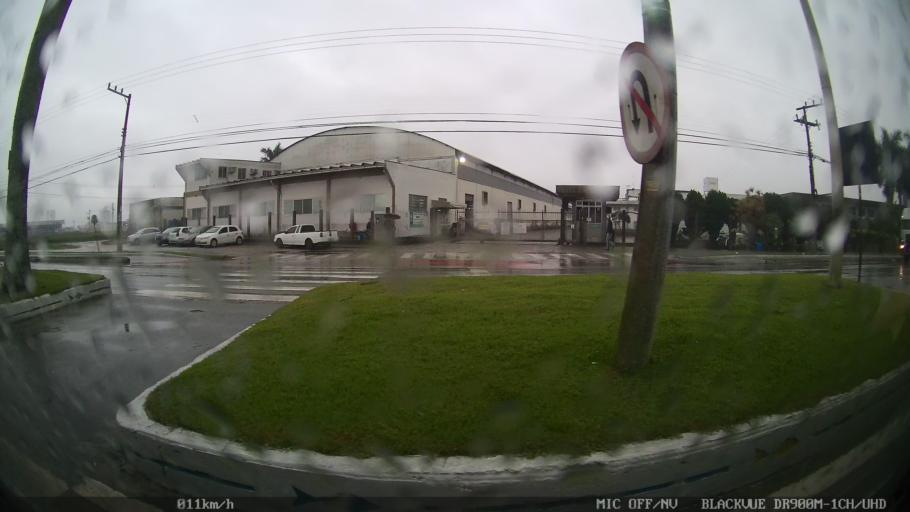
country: BR
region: Santa Catarina
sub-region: Itajai
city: Itajai
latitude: -26.9139
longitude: -48.6951
